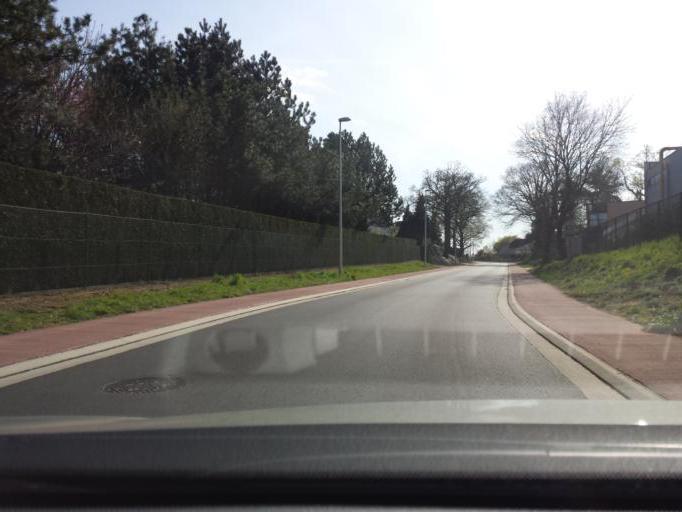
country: BE
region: Flanders
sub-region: Provincie Limburg
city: Halen
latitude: 50.9755
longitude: 5.0973
